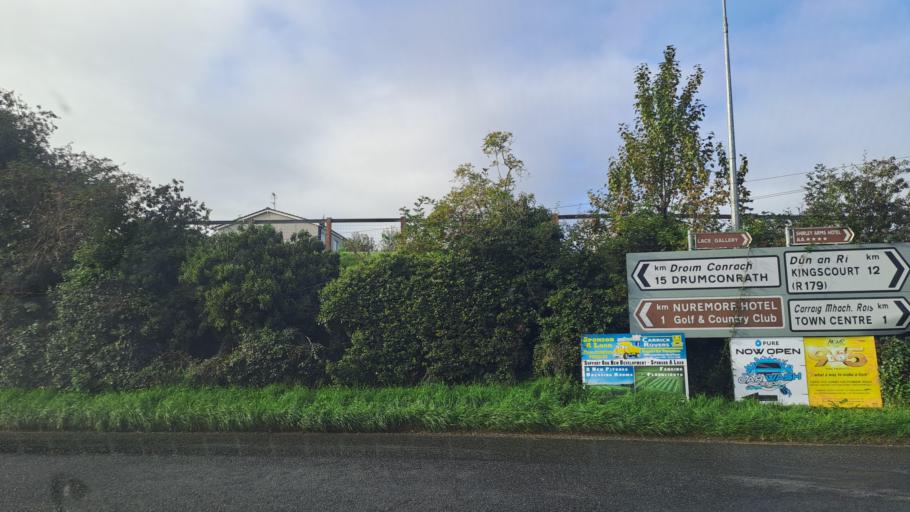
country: IE
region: Ulster
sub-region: County Monaghan
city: Carrickmacross
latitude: 53.9675
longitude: -6.7147
